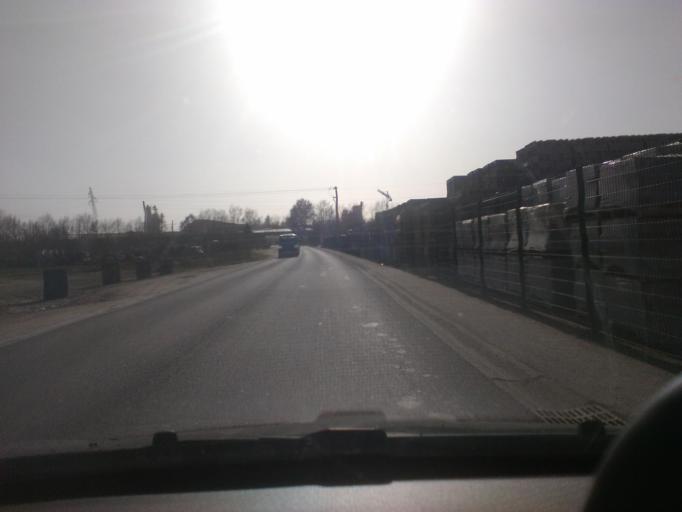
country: FR
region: Lorraine
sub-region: Departement des Vosges
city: Sainte-Marguerite
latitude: 48.2679
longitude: 6.9748
